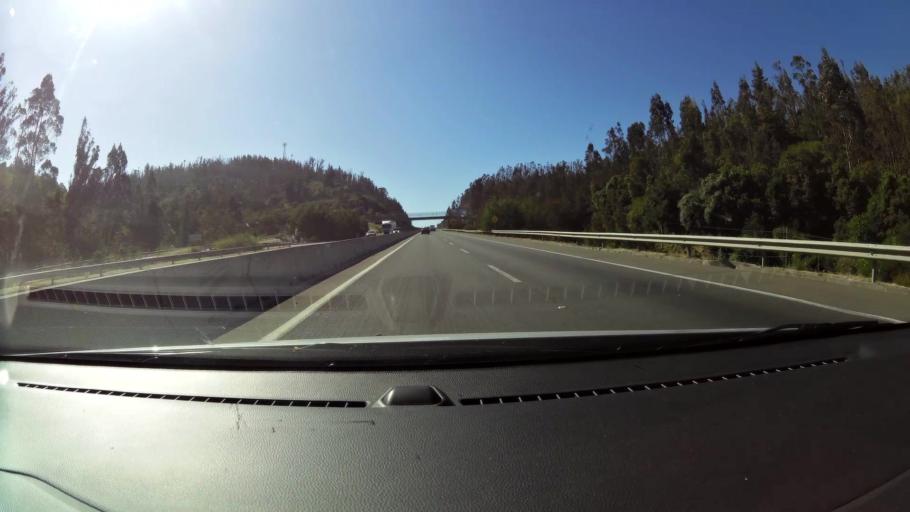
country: CL
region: Valparaiso
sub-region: Provincia de Marga Marga
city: Quilpue
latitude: -33.2102
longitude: -71.4791
